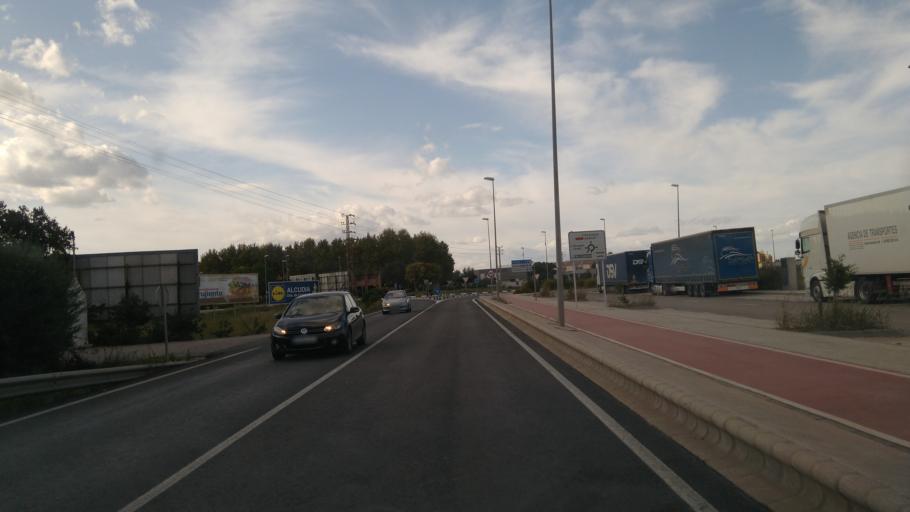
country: ES
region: Valencia
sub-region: Provincia de Valencia
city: L'Alcudia
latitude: 39.1950
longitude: -0.4977
